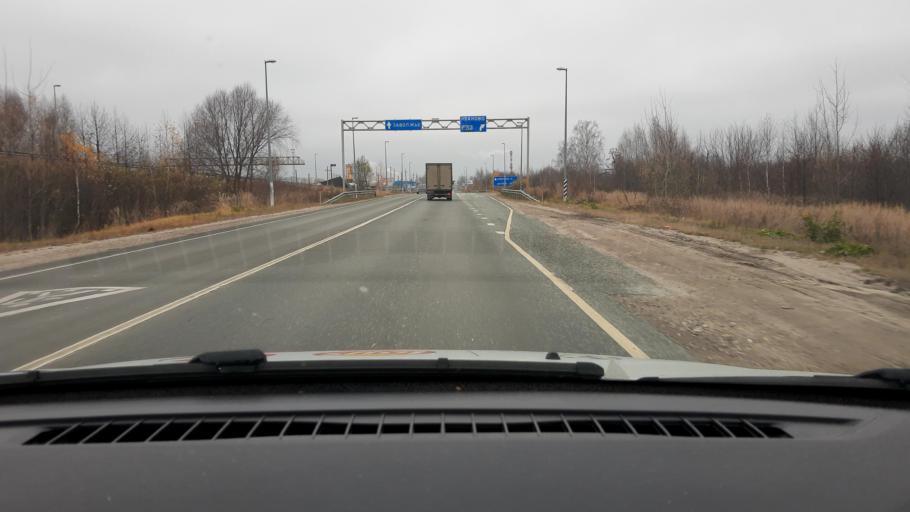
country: RU
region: Nizjnij Novgorod
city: Zavolzh'ye
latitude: 56.6179
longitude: 43.4327
